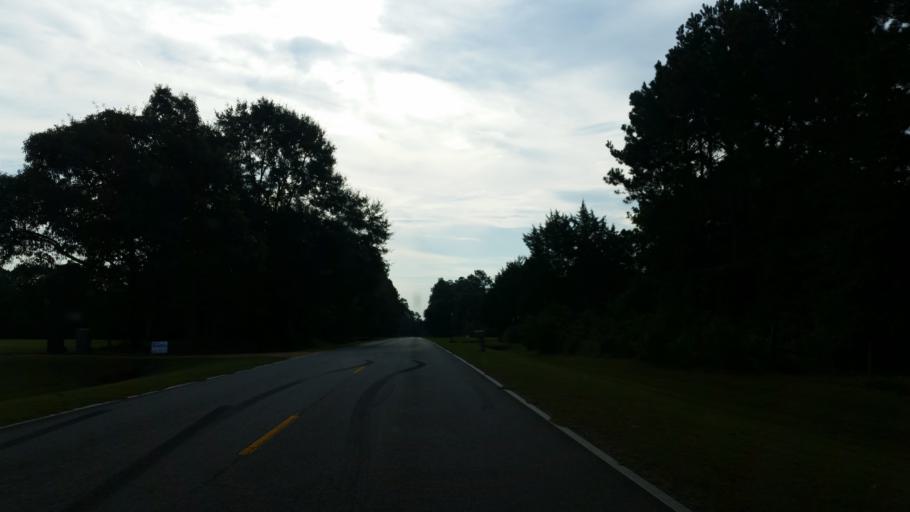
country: US
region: Florida
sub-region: Escambia County
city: Molino
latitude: 30.7709
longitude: -87.5135
